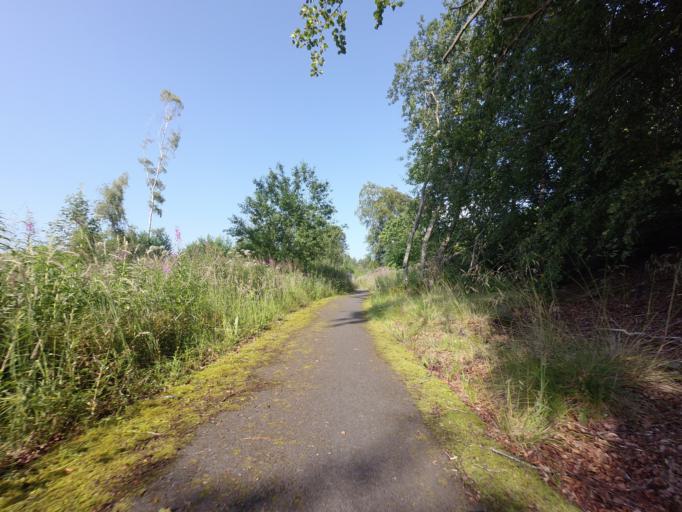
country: GB
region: Scotland
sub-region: Highland
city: Evanton
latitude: 57.6803
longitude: -4.3002
